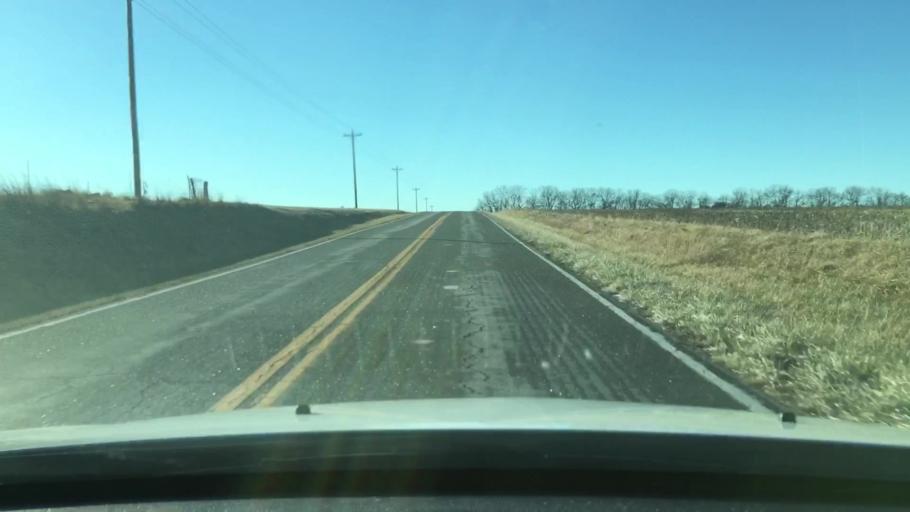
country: US
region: Missouri
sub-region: Audrain County
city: Mexico
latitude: 39.2766
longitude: -91.7862
